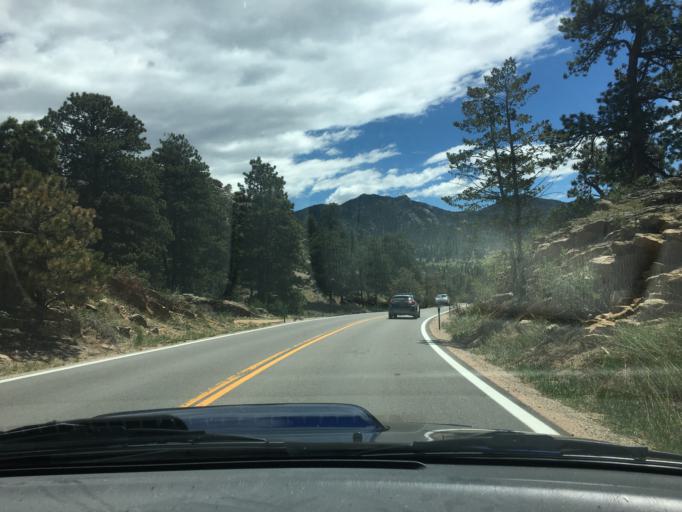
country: US
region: Colorado
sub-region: Larimer County
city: Estes Park
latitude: 40.3434
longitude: -105.5228
